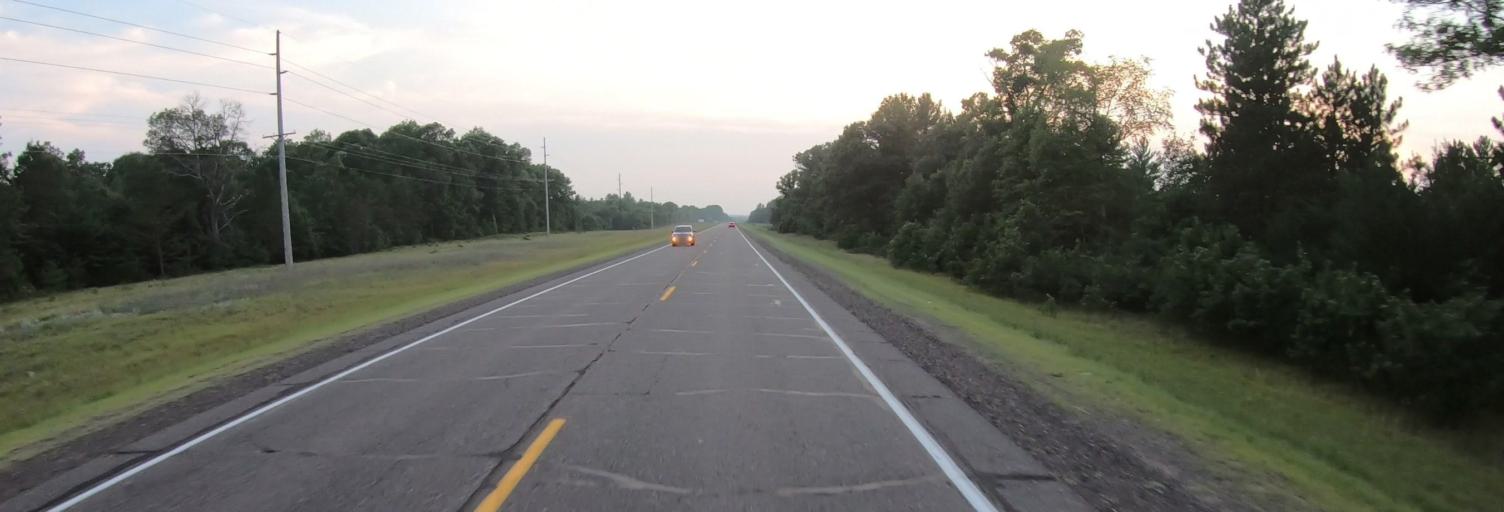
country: US
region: Wisconsin
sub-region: Burnett County
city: Grantsburg
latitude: 45.7730
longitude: -92.7513
